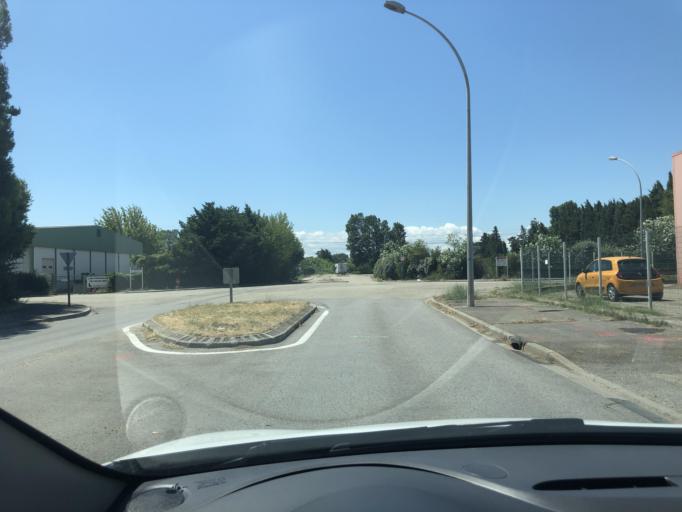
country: FR
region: Provence-Alpes-Cote d'Azur
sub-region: Departement des Bouches-du-Rhone
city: Chateaurenard
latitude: 43.8971
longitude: 4.8756
